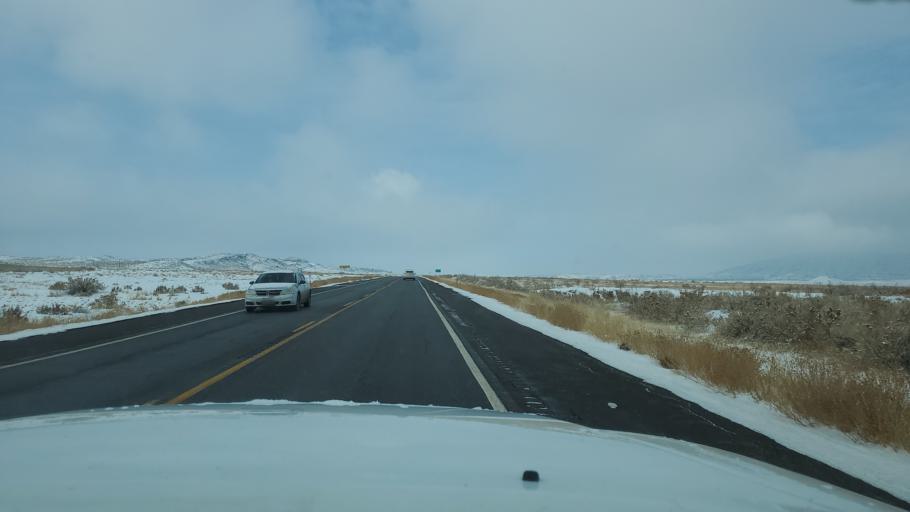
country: US
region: Utah
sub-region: Uintah County
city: Naples
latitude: 40.2894
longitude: -109.1558
